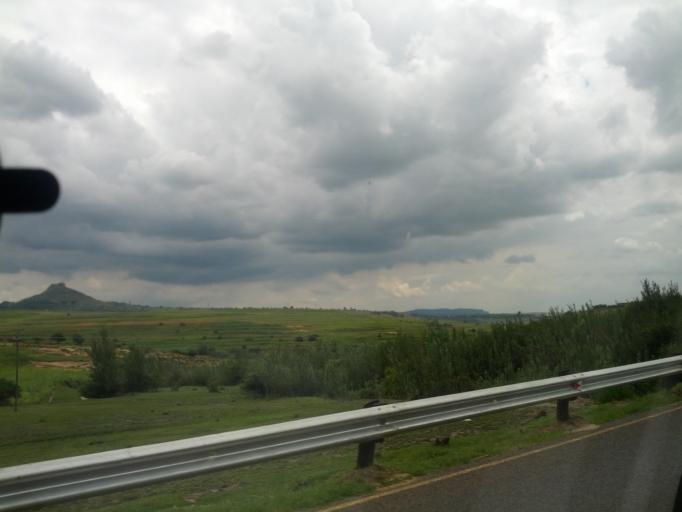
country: LS
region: Leribe
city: Leribe
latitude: -28.9724
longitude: 28.1746
